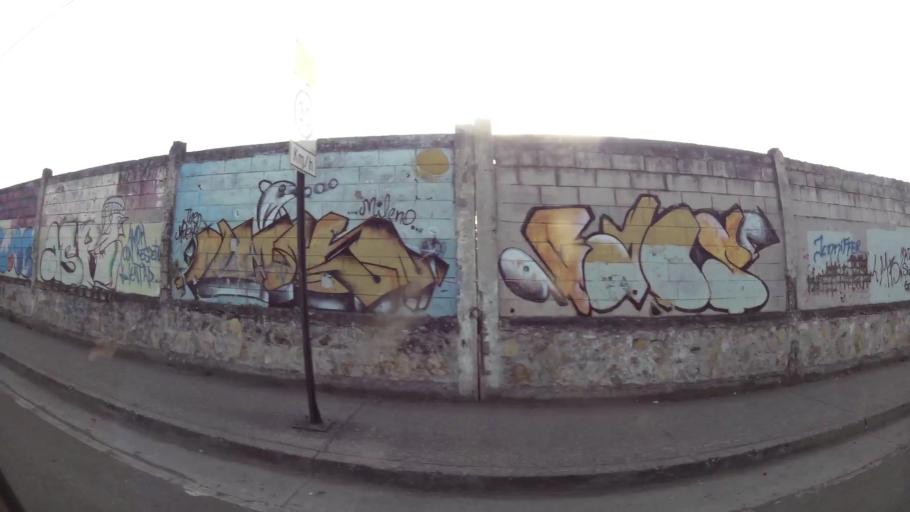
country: EC
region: Guayas
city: Guayaquil
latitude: -2.1499
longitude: -79.9127
